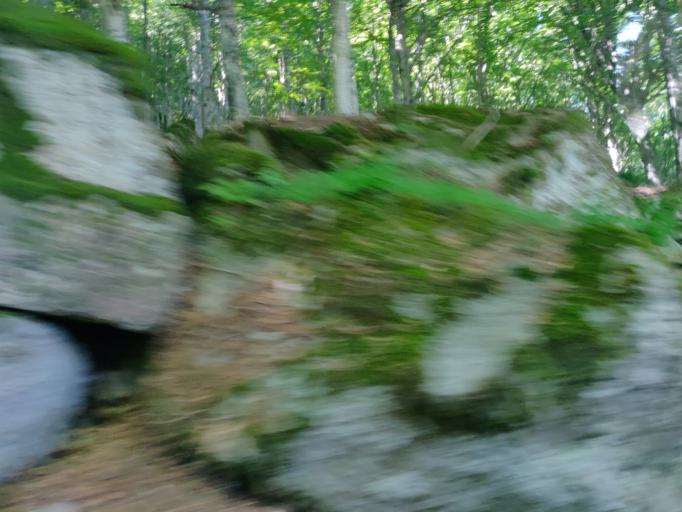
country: IT
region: Tuscany
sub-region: Provincia di Siena
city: Abbadia San Salvatore
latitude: 42.8949
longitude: 11.6305
